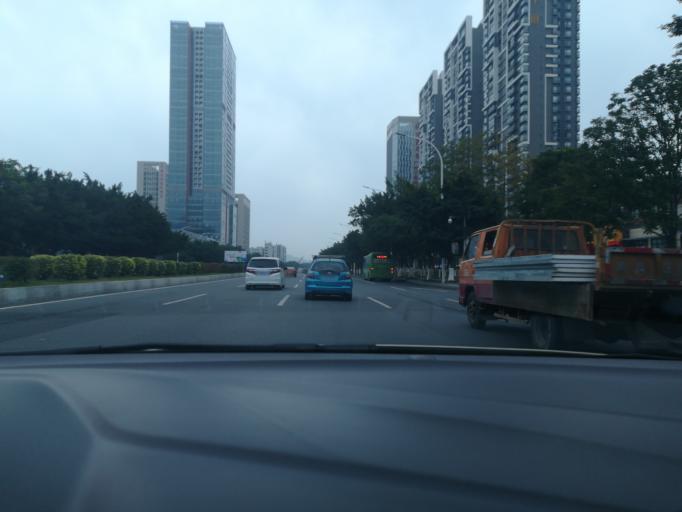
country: CN
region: Guangdong
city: Nansha
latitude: 22.8007
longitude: 113.5730
